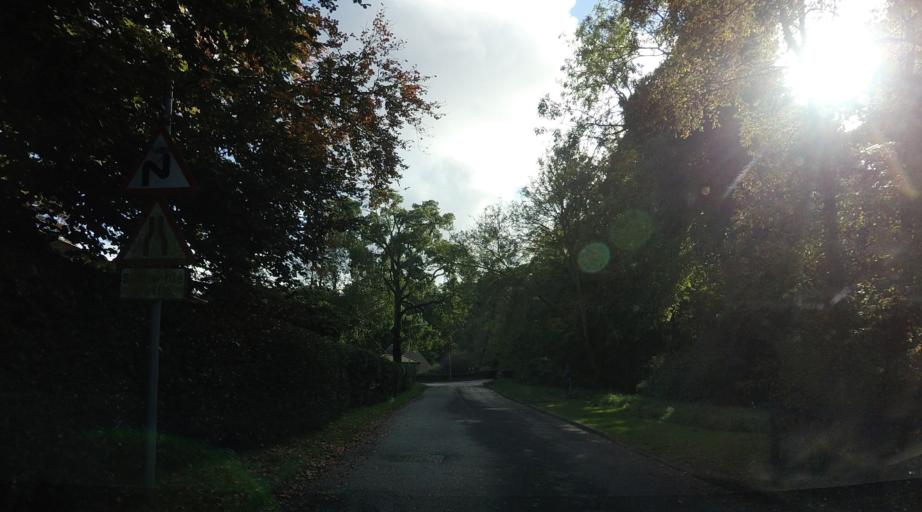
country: GB
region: Scotland
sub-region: Fife
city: Balmullo
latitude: 56.3838
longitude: -2.9949
